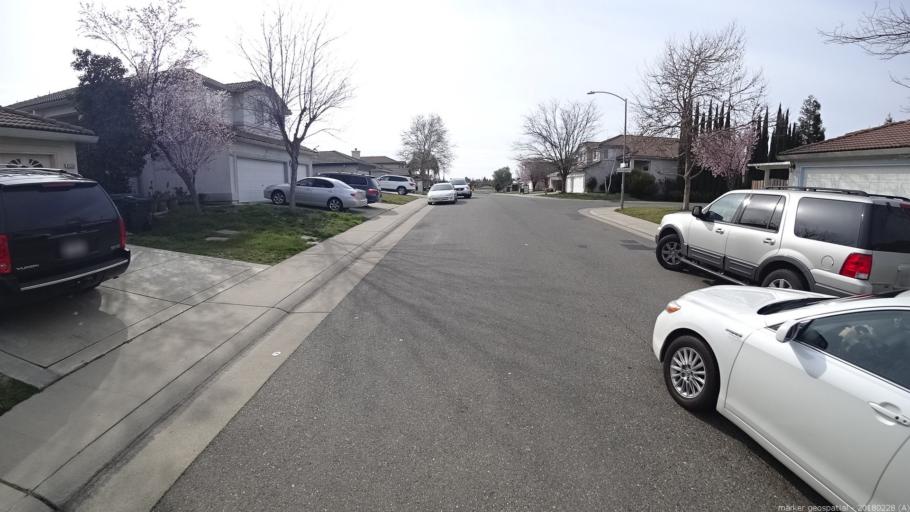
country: US
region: California
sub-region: Sacramento County
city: Antelope
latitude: 38.7190
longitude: -121.3359
